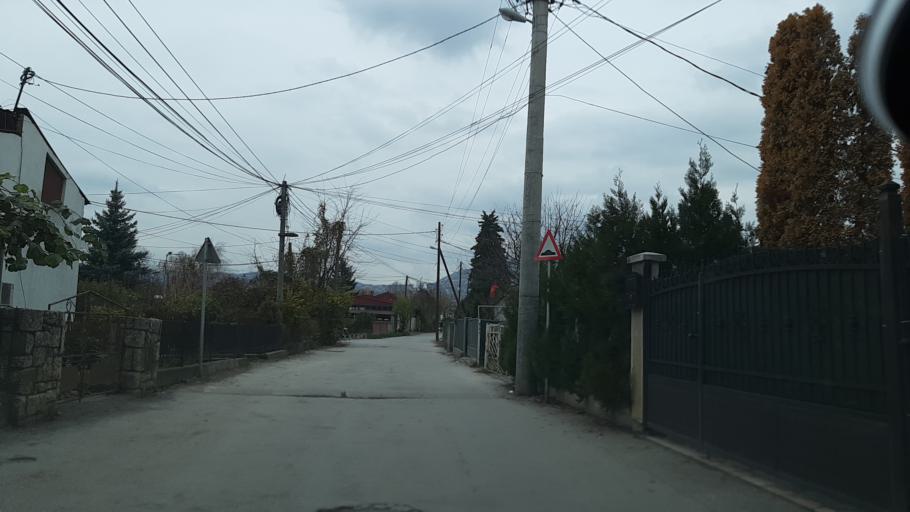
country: MK
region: Kisela Voda
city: Usje
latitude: 41.9768
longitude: 21.4750
